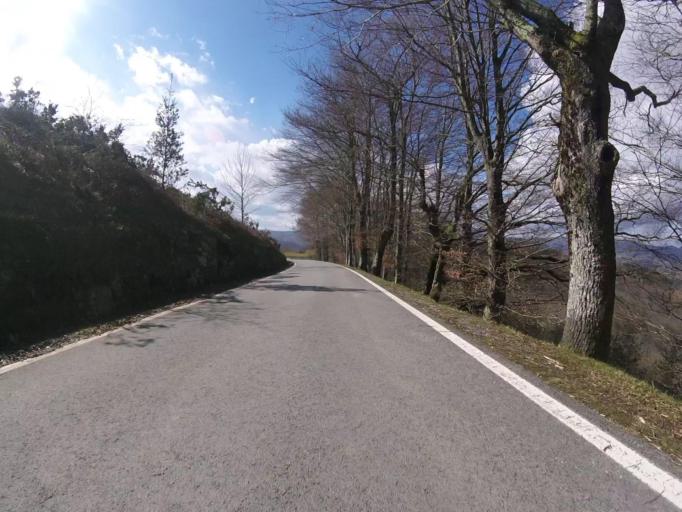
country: ES
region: Navarre
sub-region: Provincia de Navarra
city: Etxalar
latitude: 43.2578
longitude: -1.6229
